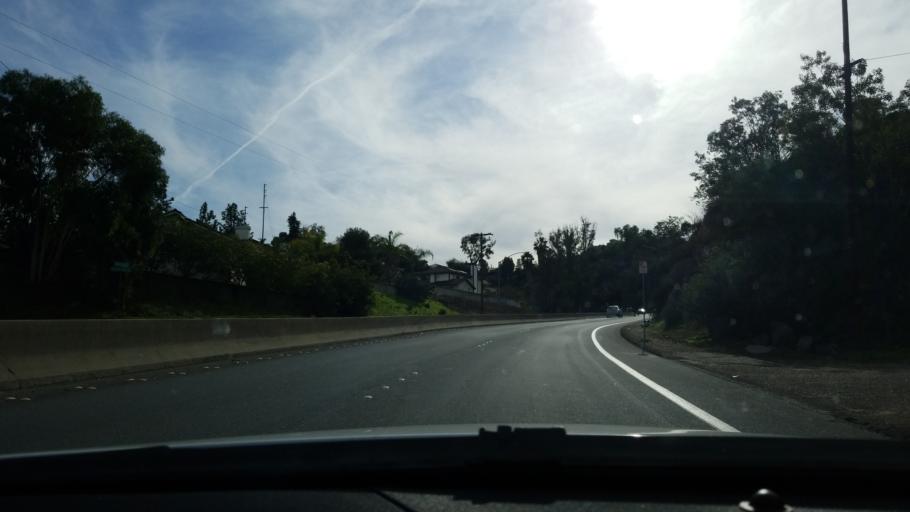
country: US
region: California
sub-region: San Diego County
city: Casa de Oro-Mount Helix
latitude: 32.7771
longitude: -116.9581
